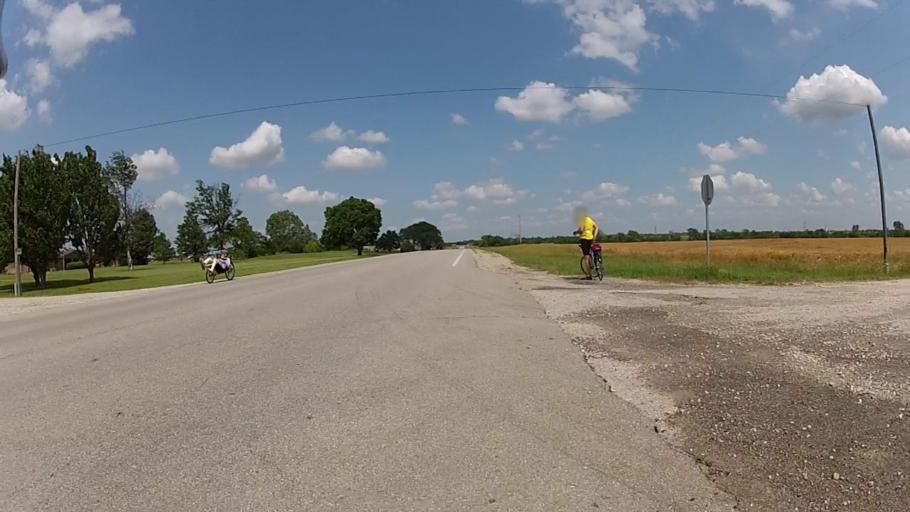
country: US
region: Kansas
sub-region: Labette County
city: Oswego
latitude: 37.1934
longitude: -95.1584
